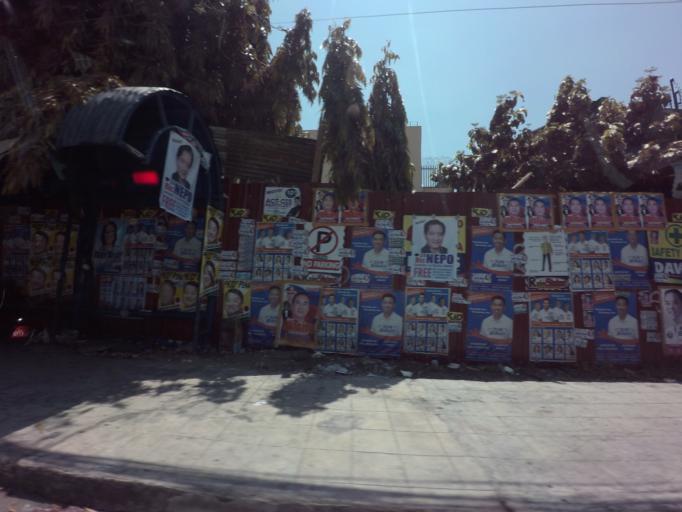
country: PH
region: Metro Manila
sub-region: Makati City
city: Makati City
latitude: 14.5609
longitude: 121.0029
